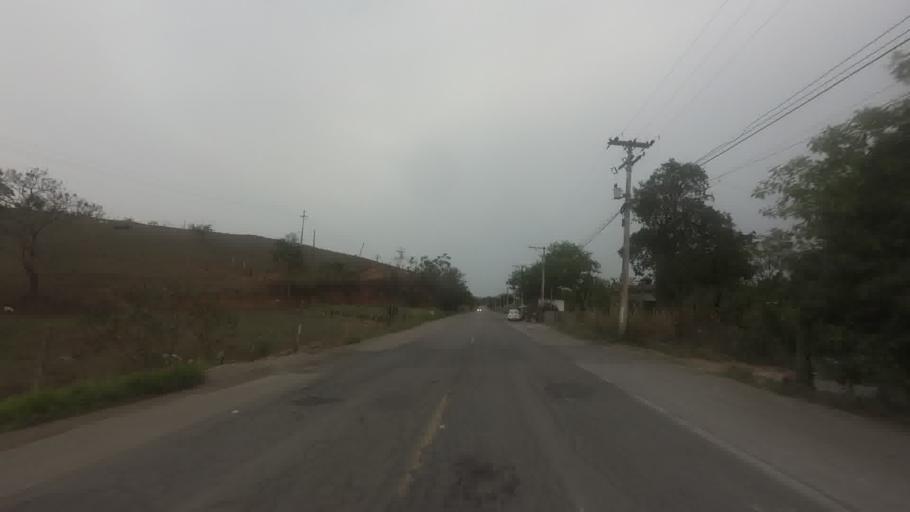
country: BR
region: Rio de Janeiro
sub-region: Santo Antonio De Padua
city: Santo Antonio de Padua
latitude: -21.6405
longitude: -42.2787
